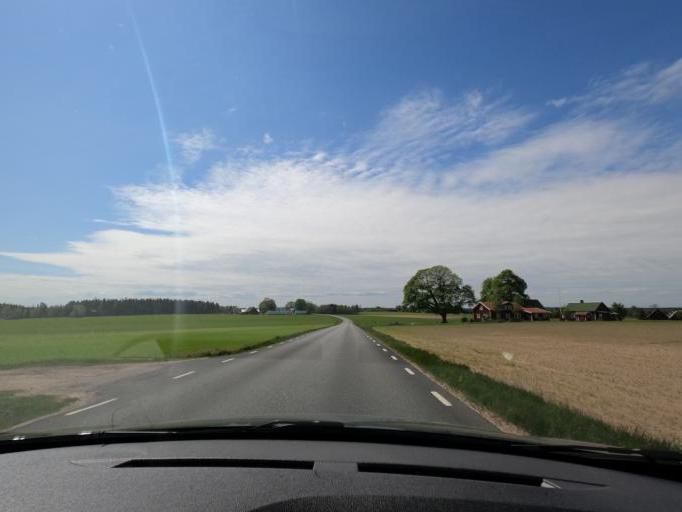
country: SE
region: Joenkoeping
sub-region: Varnamo Kommun
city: Bredaryd
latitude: 57.1435
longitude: 13.7170
